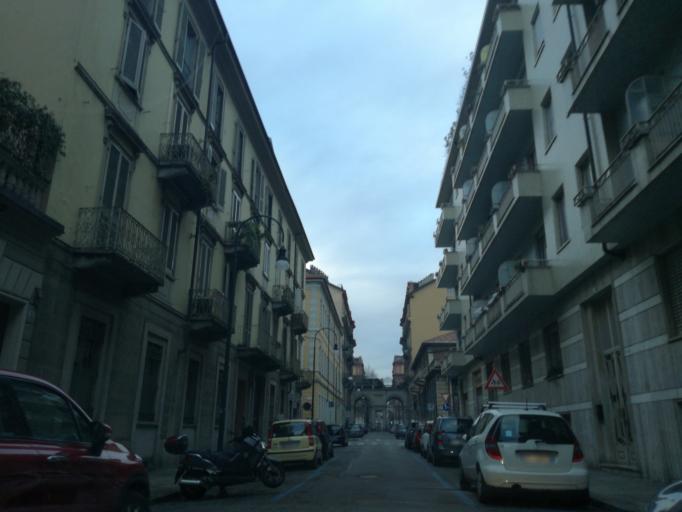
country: IT
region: Piedmont
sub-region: Provincia di Torino
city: Turin
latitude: 45.0775
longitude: 7.6720
